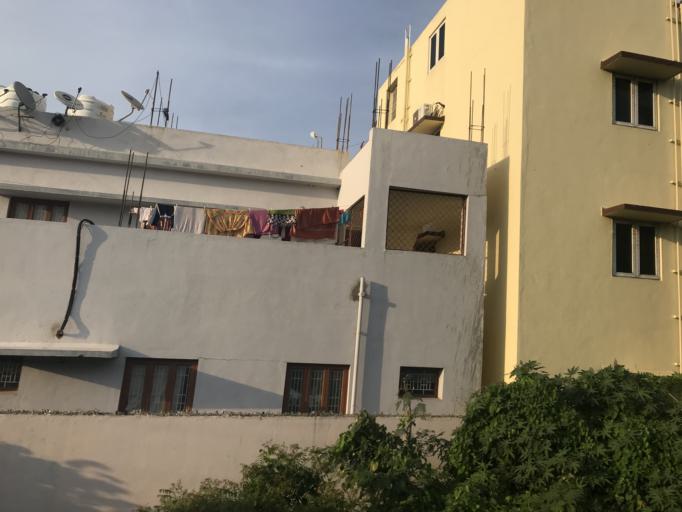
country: IN
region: Tamil Nadu
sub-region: Coimbatore
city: Coimbatore
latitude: 11.0312
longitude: 76.9664
